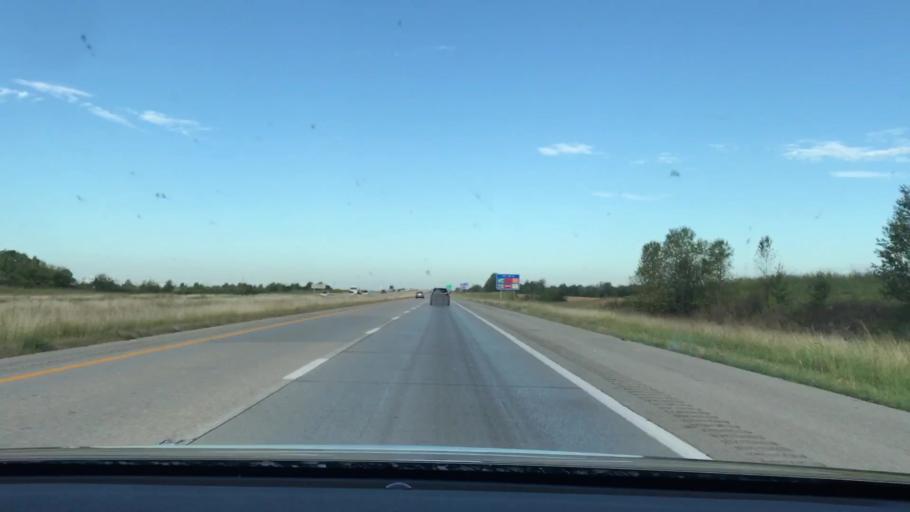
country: US
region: Kentucky
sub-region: Christian County
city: Oak Grove
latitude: 36.6966
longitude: -87.4386
